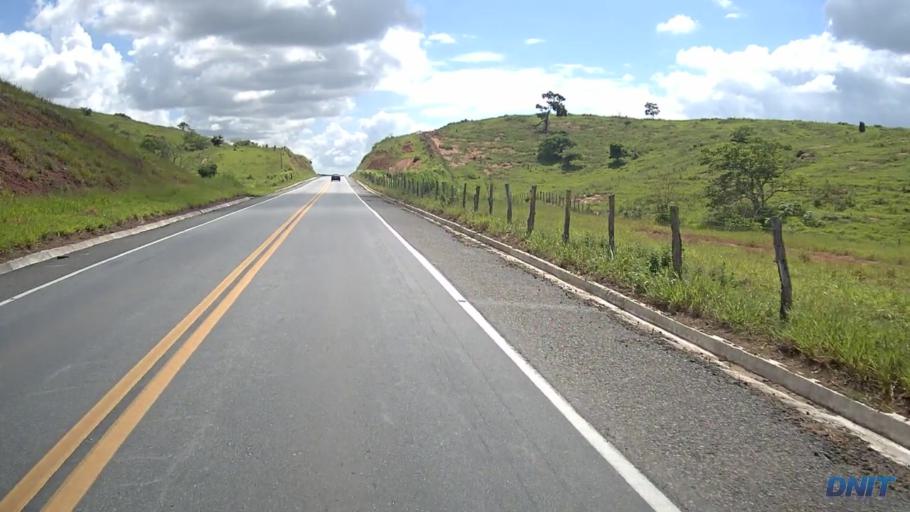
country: BR
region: Minas Gerais
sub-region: Governador Valadares
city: Governador Valadares
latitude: -18.9919
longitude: -42.1155
